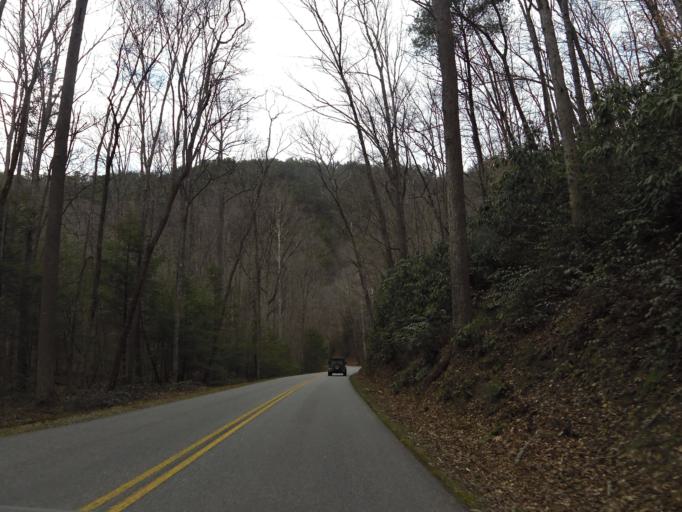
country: US
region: Tennessee
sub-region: Sevier County
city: Pigeon Forge
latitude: 35.6689
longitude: -83.6787
